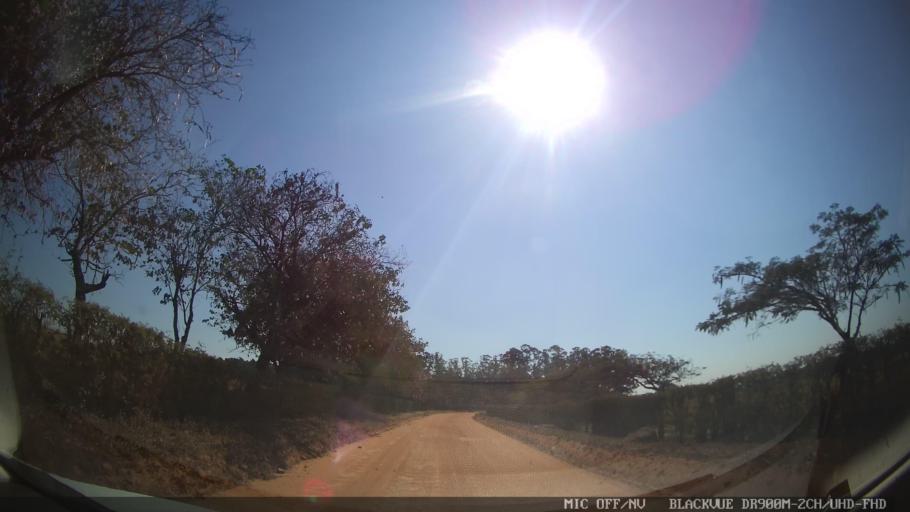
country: BR
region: Sao Paulo
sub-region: Itupeva
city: Itupeva
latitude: -23.0740
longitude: -47.0934
